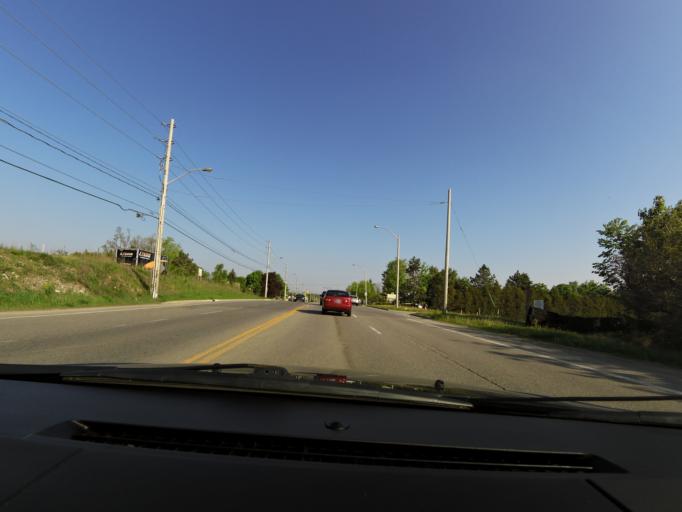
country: CA
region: Ontario
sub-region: Wellington County
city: Guelph
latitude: 43.4979
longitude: -80.1857
